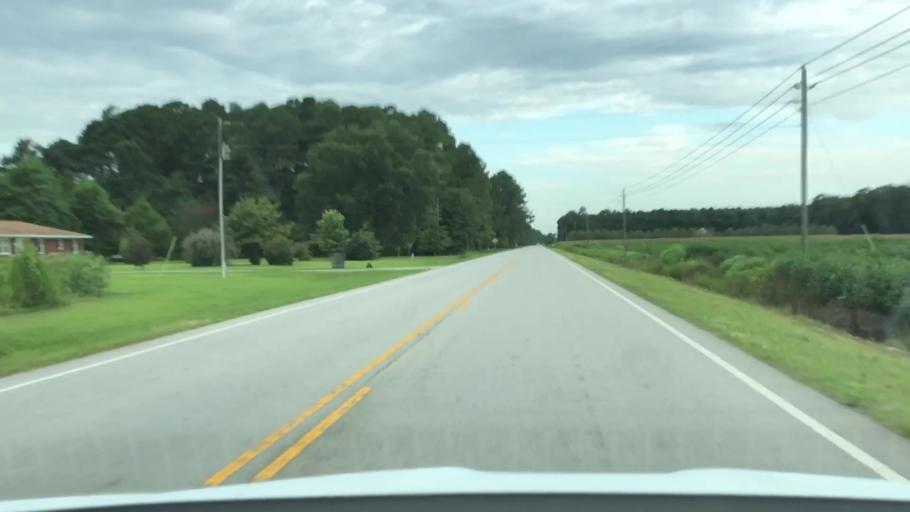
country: US
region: North Carolina
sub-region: Jones County
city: Trenton
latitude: 35.0704
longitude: -77.3735
